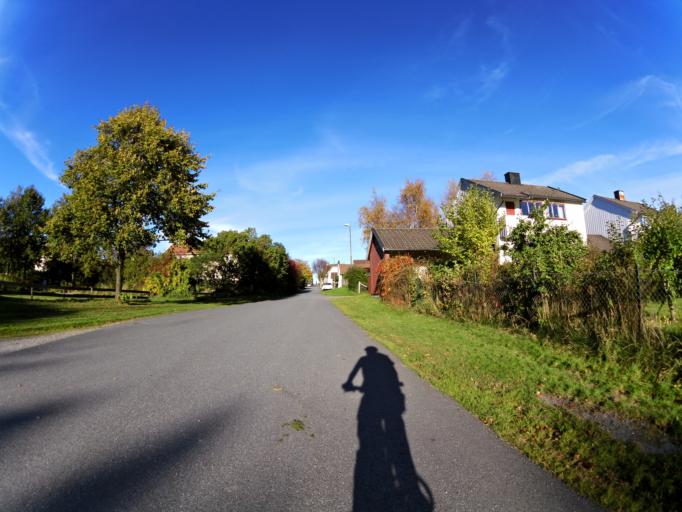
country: NO
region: Ostfold
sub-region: Sarpsborg
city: Sarpsborg
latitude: 59.2778
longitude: 11.1160
